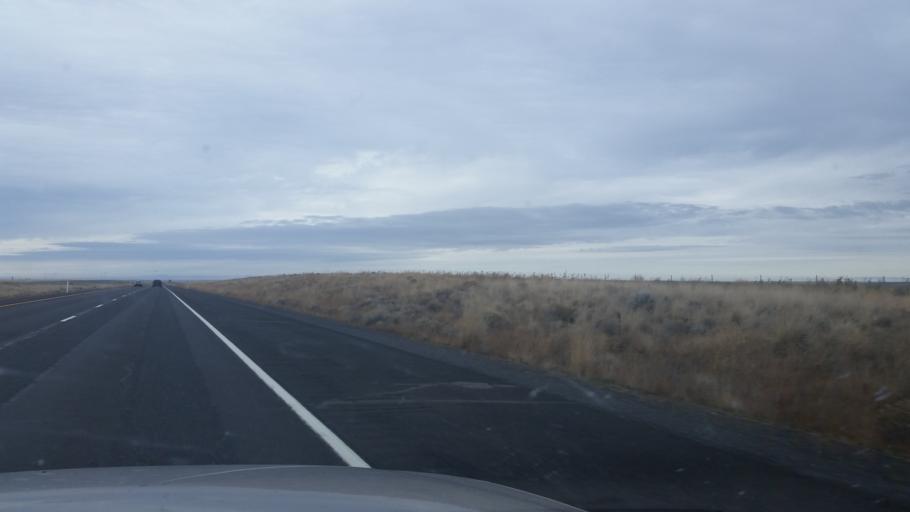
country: US
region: Washington
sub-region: Adams County
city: Ritzville
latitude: 47.1115
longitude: -118.4732
